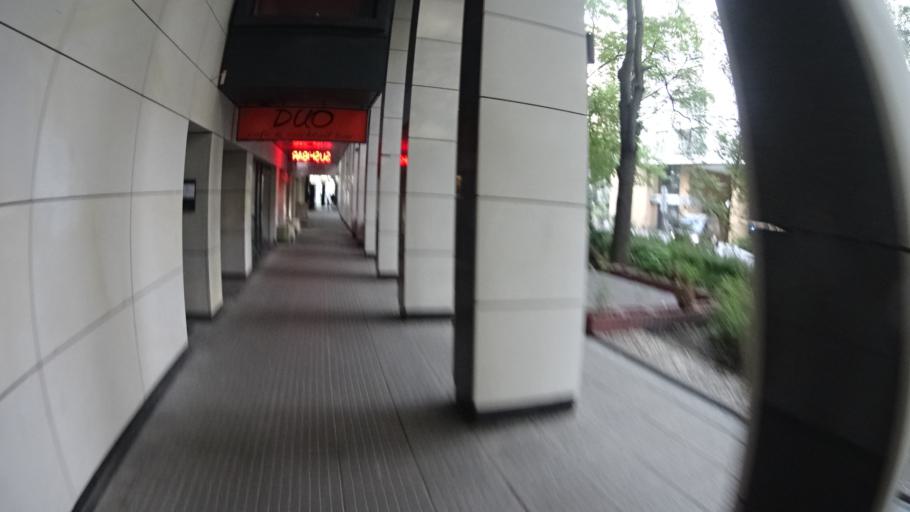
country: PL
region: Masovian Voivodeship
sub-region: Warszawa
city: Warsaw
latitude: 52.2381
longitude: 21.0026
